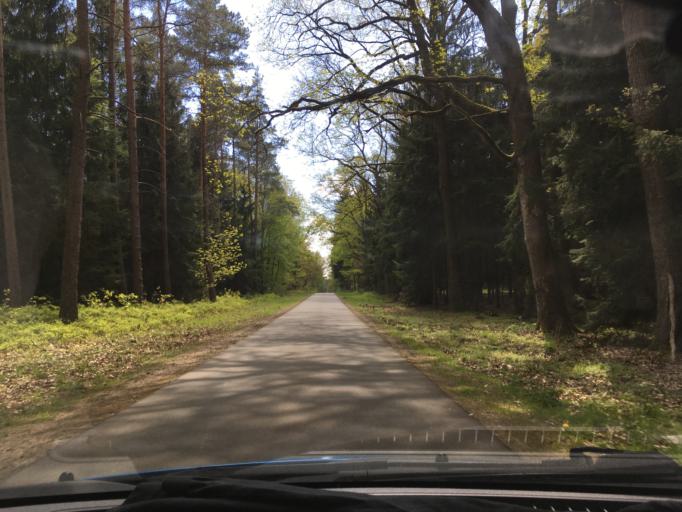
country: DE
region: Lower Saxony
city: Boitze
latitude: 53.1184
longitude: 10.7909
